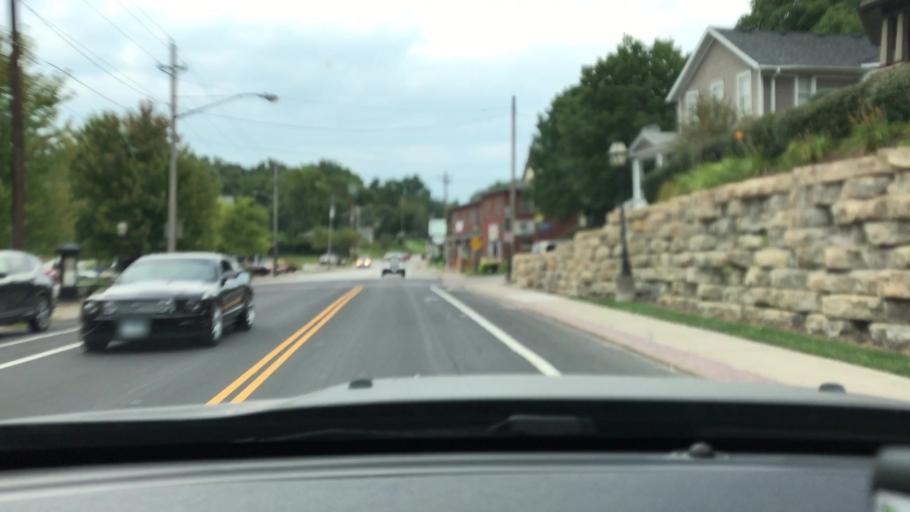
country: US
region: Iowa
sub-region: Scott County
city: Bettendorf
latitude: 41.5316
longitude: -90.5435
